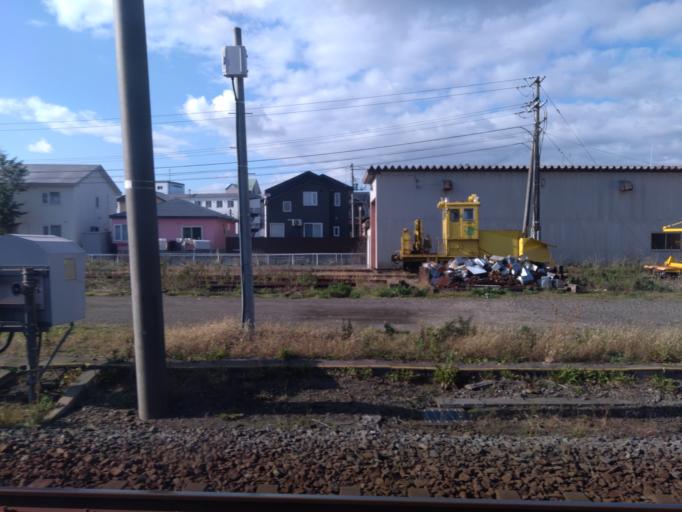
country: JP
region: Hokkaido
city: Muroran
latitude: 42.3516
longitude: 141.0296
